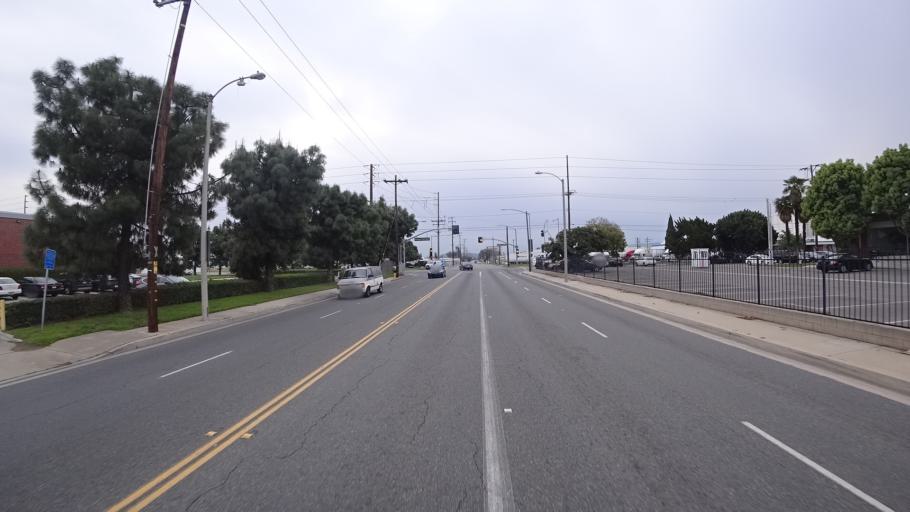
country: US
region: California
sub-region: Los Angeles County
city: Avocado Heights
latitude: 34.0577
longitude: -117.9924
